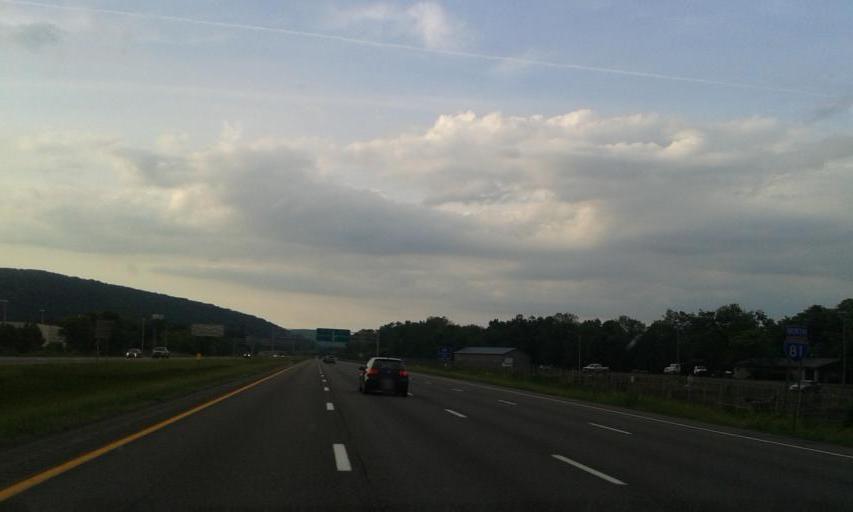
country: US
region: New York
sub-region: Broome County
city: Port Dickinson
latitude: 42.1301
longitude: -75.9038
